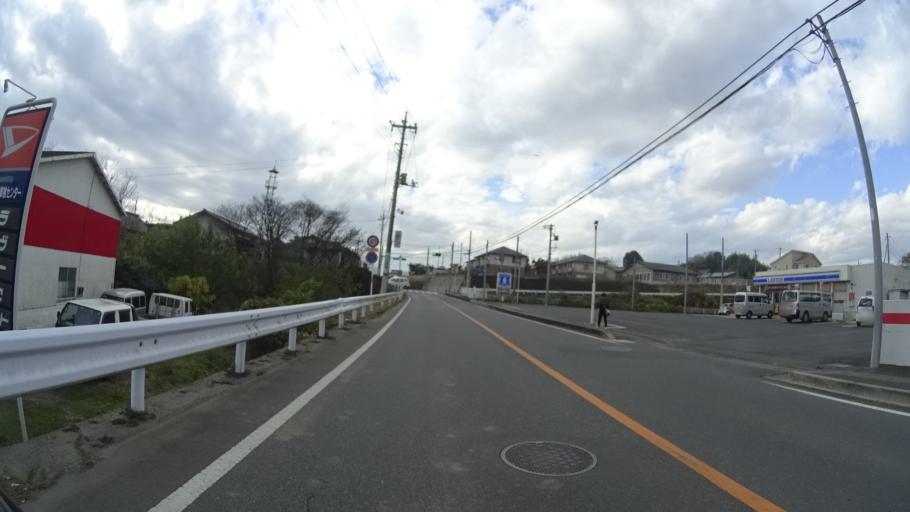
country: JP
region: Gunma
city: Maebashi-shi
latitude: 36.4170
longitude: 139.1538
